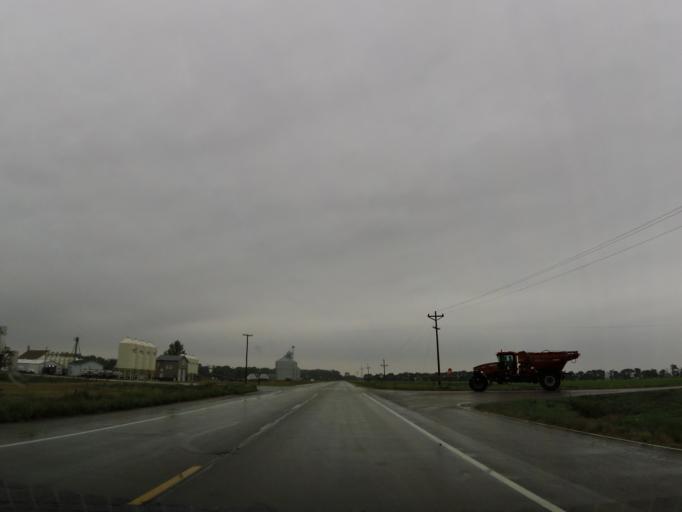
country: US
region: Minnesota
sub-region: Marshall County
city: Warren
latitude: 48.4556
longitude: -96.8704
